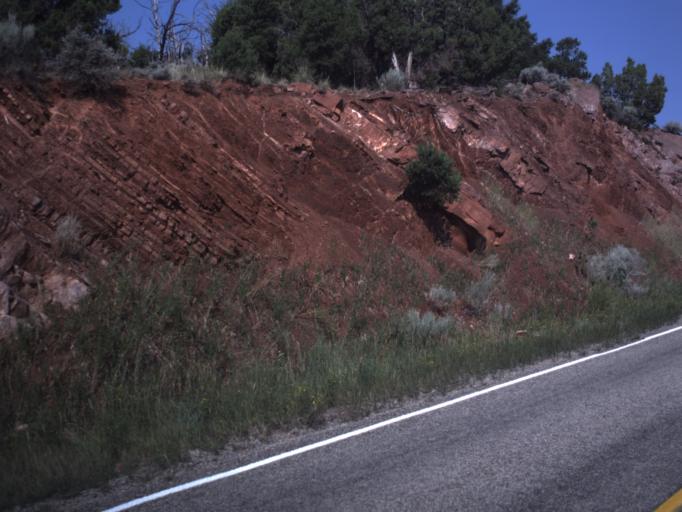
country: US
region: Utah
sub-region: Daggett County
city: Manila
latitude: 40.9391
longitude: -109.4089
